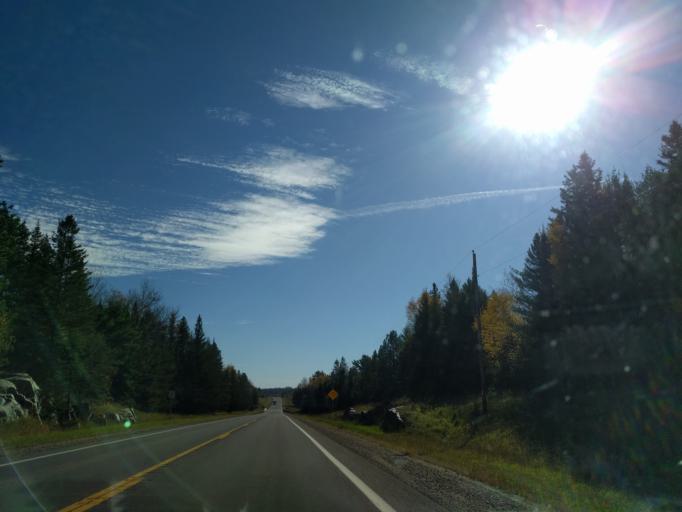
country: US
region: Michigan
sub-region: Marquette County
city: West Ishpeming
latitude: 46.3775
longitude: -87.9921
